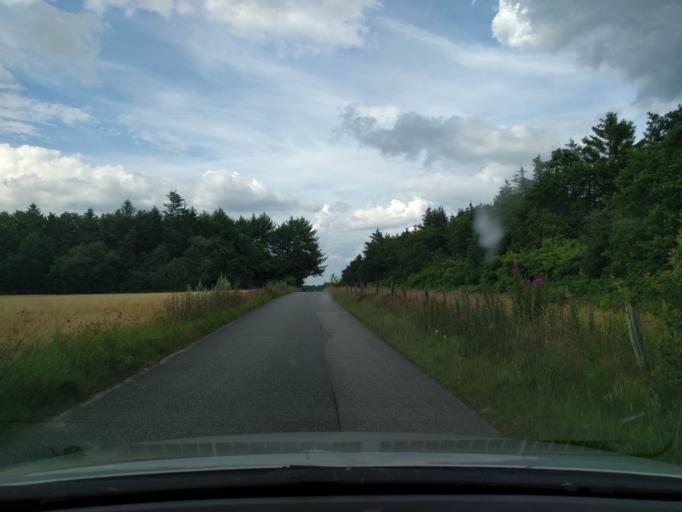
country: DK
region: Central Jutland
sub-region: Herning Kommune
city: Kibaek
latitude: 56.0770
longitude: 8.8950
